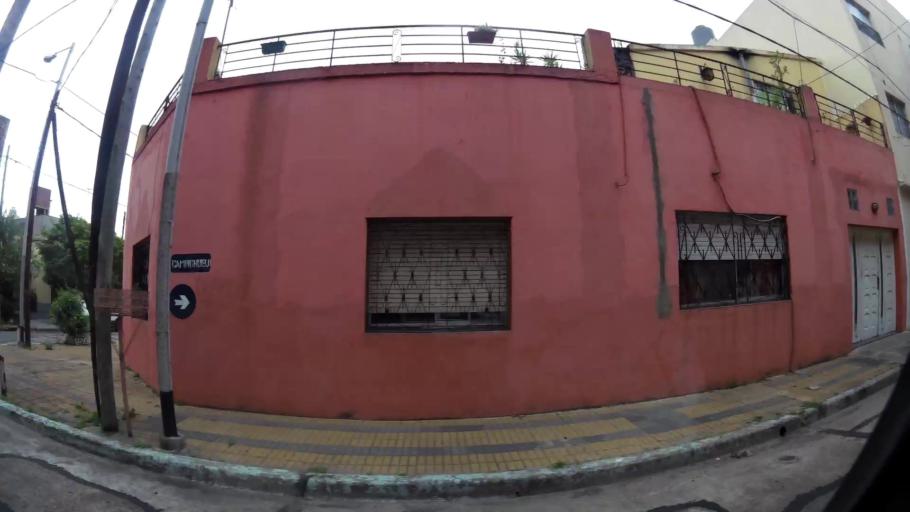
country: AR
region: Buenos Aires
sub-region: Partido de Lanus
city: Lanus
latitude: -34.6829
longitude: -58.3834
